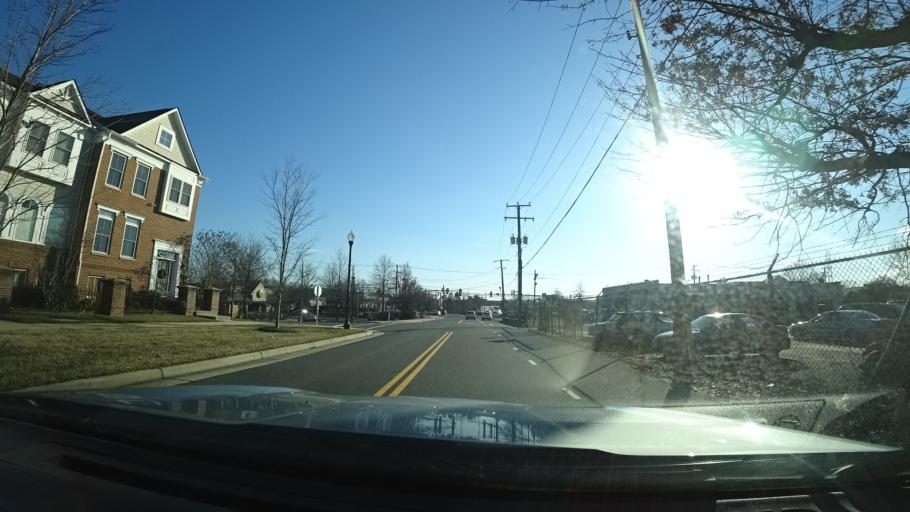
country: US
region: Virginia
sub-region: Fairfax County
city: Herndon
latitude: 38.9699
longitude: -77.3804
